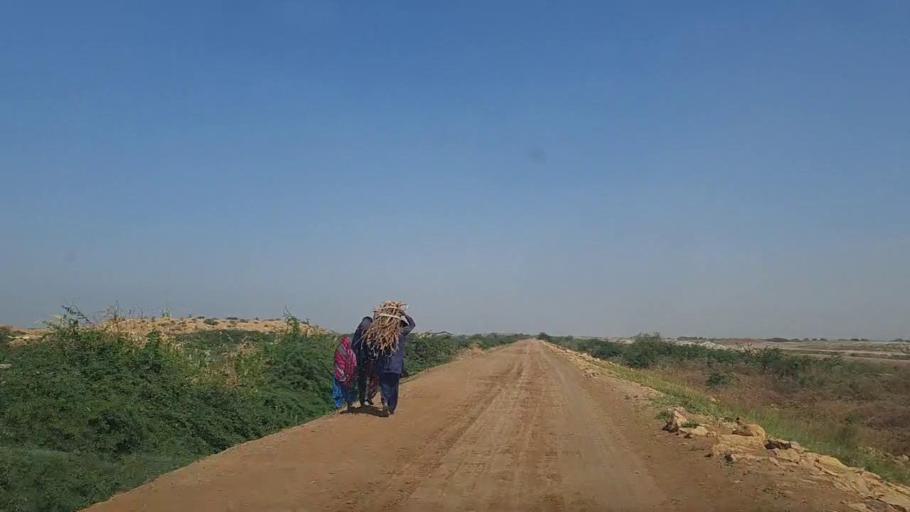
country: PK
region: Sindh
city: Daro Mehar
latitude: 24.8758
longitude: 68.0515
